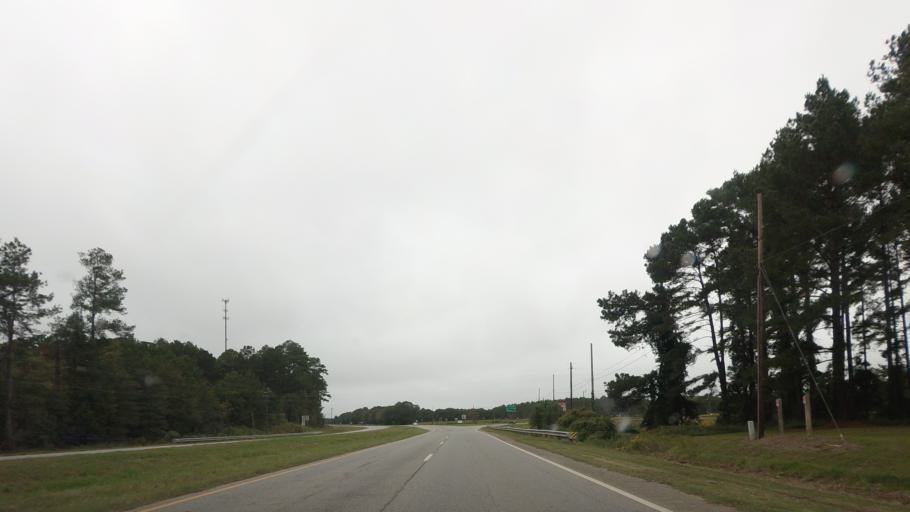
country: US
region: Georgia
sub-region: Berrien County
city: Enigma
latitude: 31.3945
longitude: -83.2364
